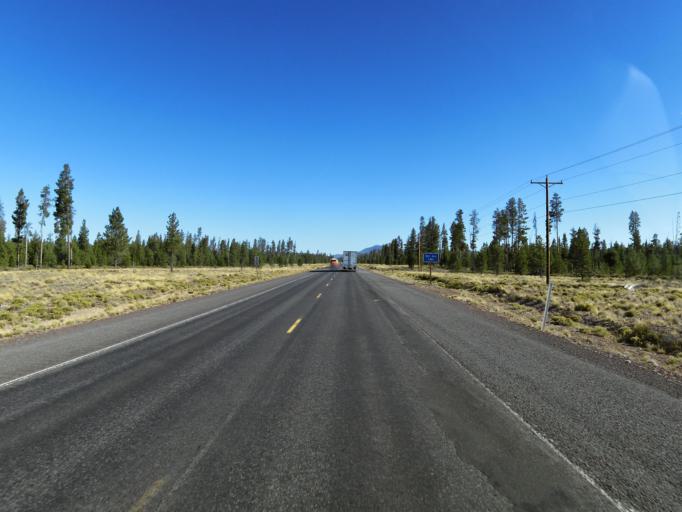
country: US
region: Oregon
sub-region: Deschutes County
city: La Pine
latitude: 43.1564
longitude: -121.7937
